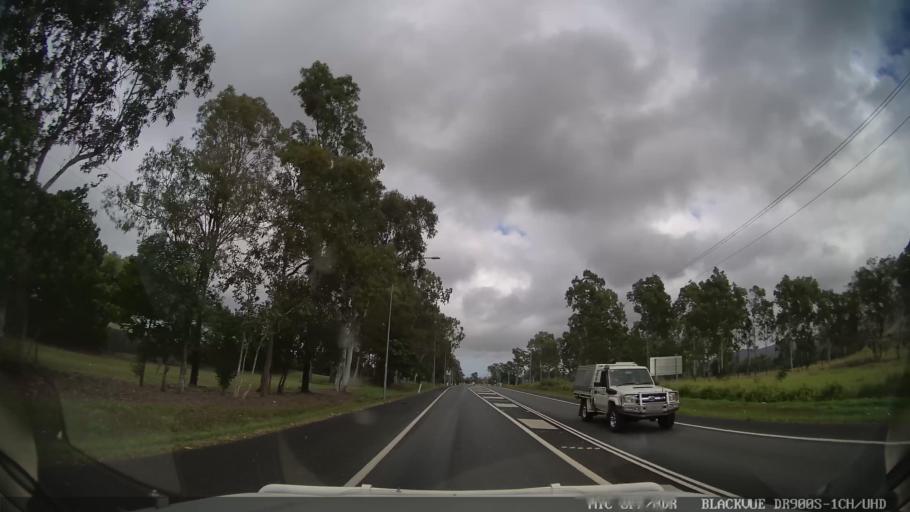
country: AU
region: Queensland
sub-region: Whitsunday
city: Proserpine
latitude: -20.3066
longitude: 148.6619
